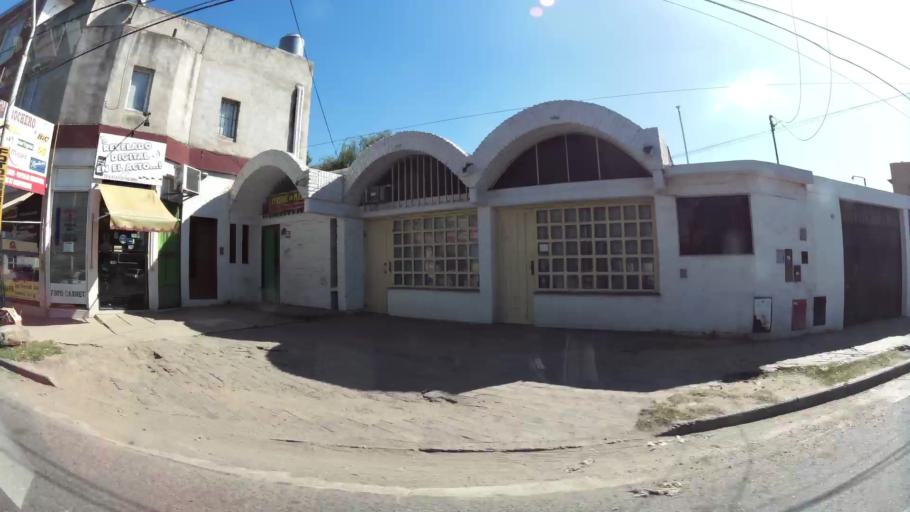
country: AR
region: Cordoba
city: Villa Allende
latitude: -31.3293
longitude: -64.2656
